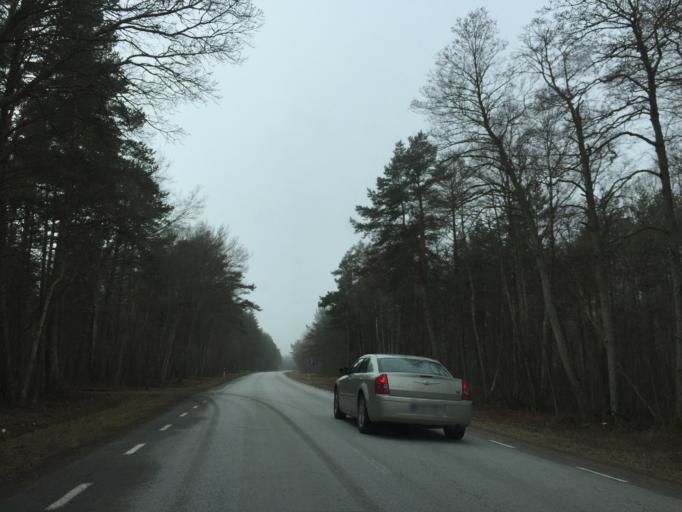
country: EE
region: Saare
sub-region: Kuressaare linn
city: Kuressaare
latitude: 58.2059
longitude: 22.2996
